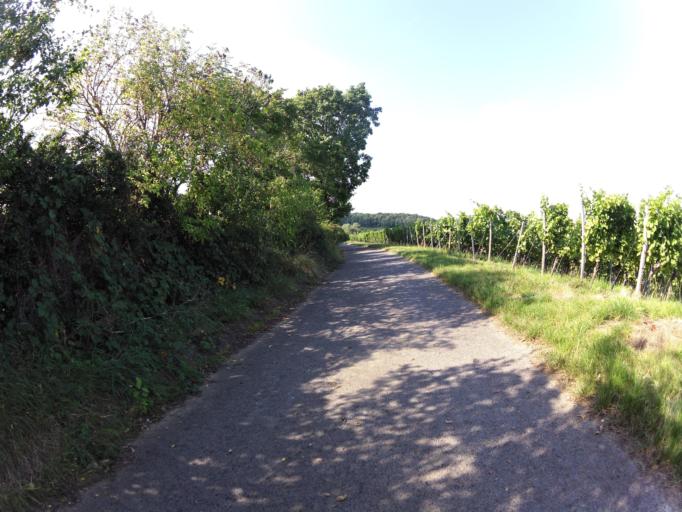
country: DE
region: Bavaria
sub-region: Regierungsbezirk Unterfranken
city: Nordheim
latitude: 49.8369
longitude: 10.1719
